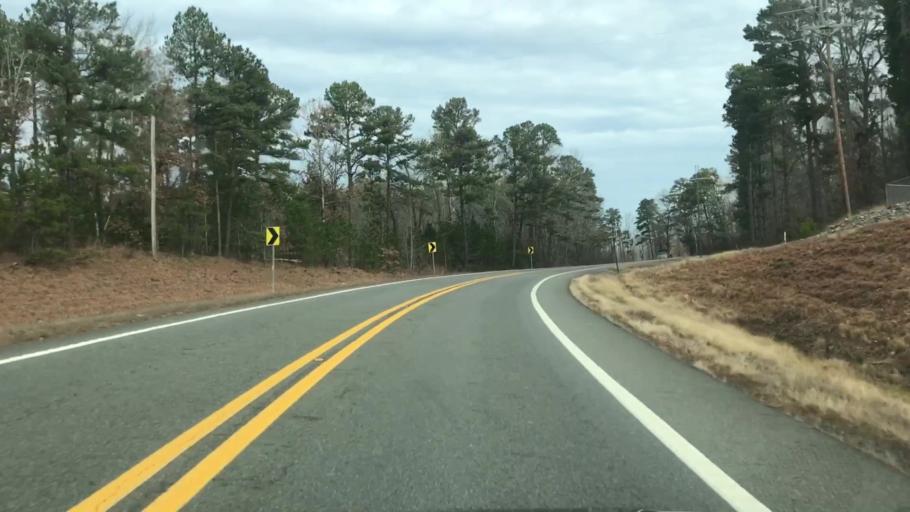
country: US
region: Arkansas
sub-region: Montgomery County
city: Mount Ida
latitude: 34.6136
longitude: -93.7034
